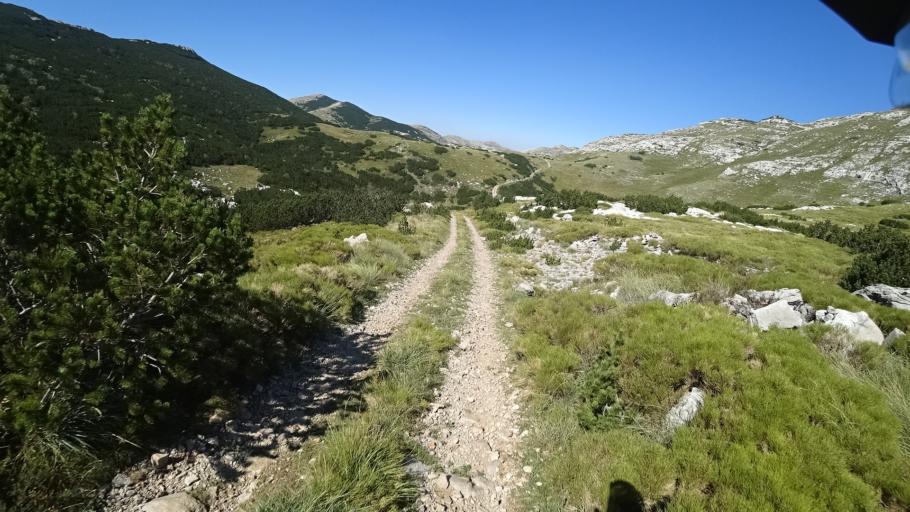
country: HR
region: Splitsko-Dalmatinska
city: Hrvace
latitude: 43.9376
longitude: 16.5901
